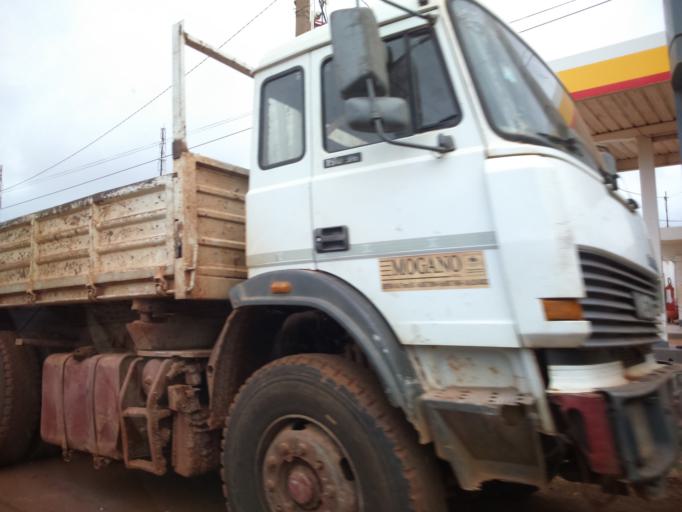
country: CI
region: Moyen-Comoe
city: Abengourou
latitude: 6.7273
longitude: -3.4971
